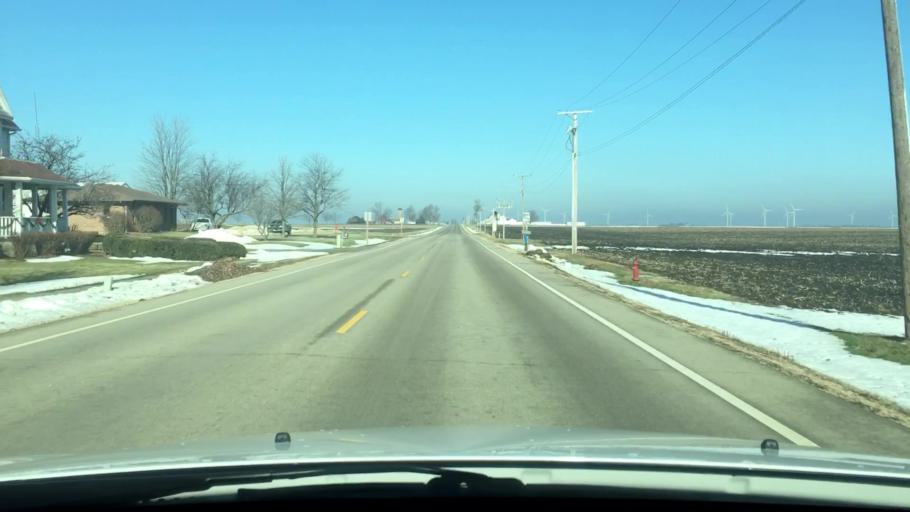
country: US
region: Illinois
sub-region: DeKalb County
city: Waterman
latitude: 41.7704
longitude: -88.8771
